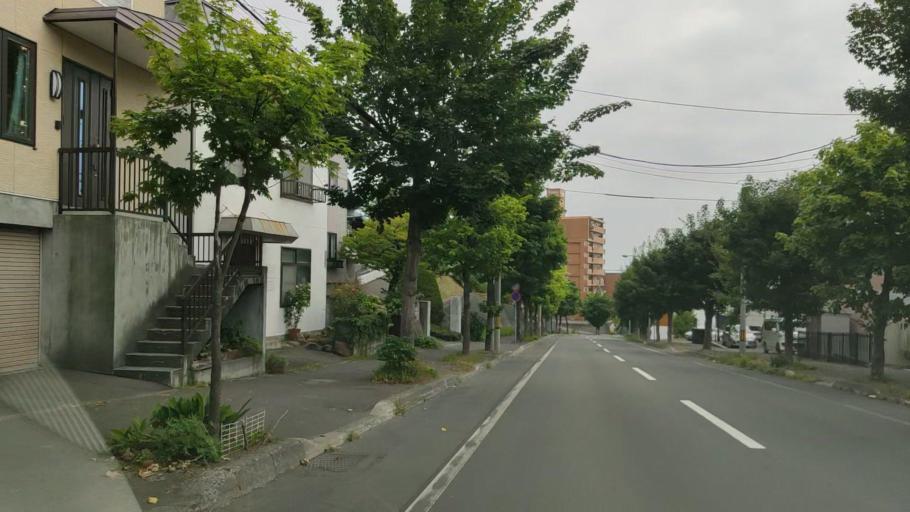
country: JP
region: Hokkaido
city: Otaru
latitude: 43.1912
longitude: 140.9851
